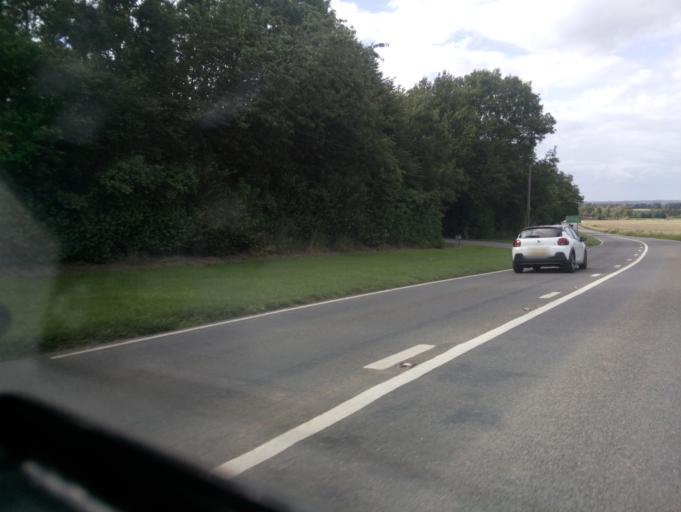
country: GB
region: England
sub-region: Leicestershire
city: Measham
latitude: 52.6674
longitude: -1.5385
